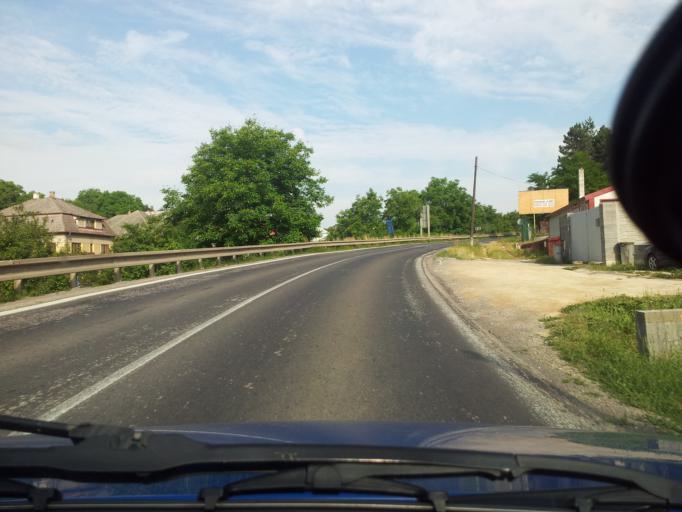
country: SK
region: Nitriansky
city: Partizanske
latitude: 48.6888
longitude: 18.3739
